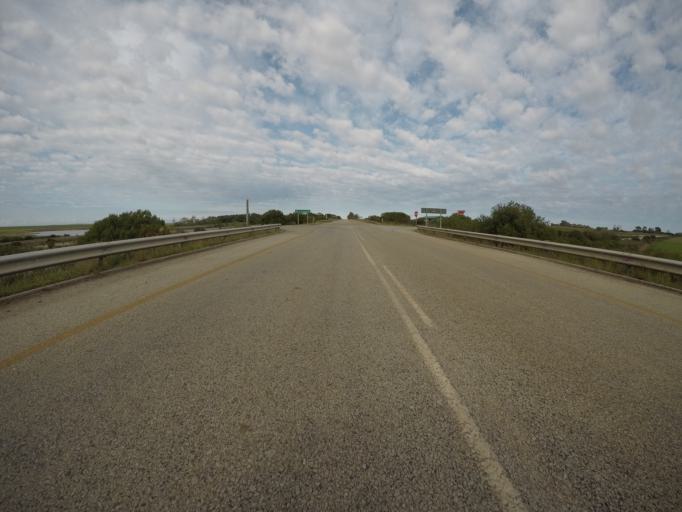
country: ZA
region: Eastern Cape
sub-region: Cacadu District Municipality
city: Kareedouw
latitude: -34.0495
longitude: 24.4564
